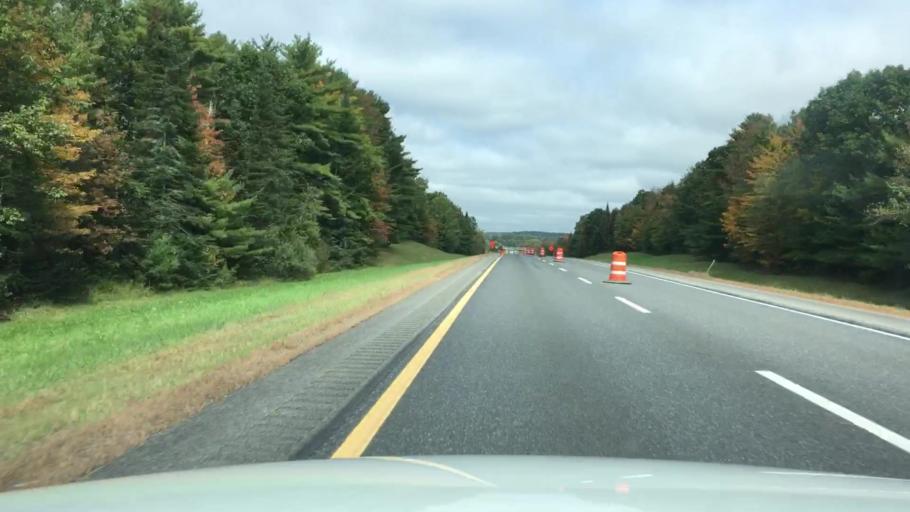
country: US
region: Maine
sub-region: Sagadahoc County
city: Richmond
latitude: 44.1403
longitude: -69.8425
